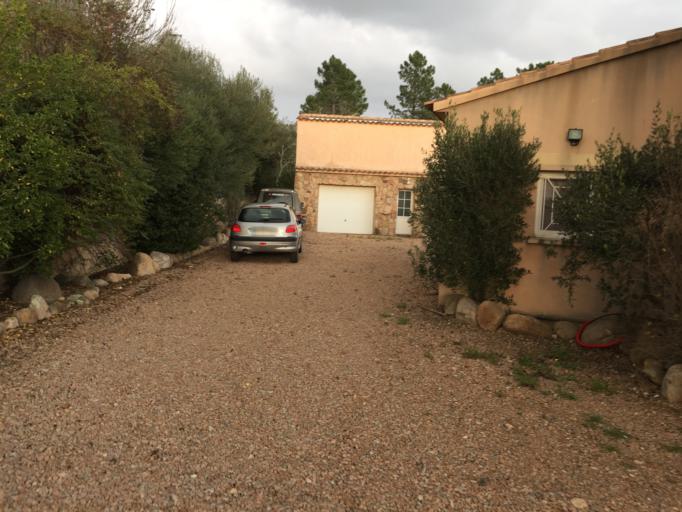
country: FR
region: Corsica
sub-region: Departement de la Corse-du-Sud
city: Porto-Vecchio
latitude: 41.6506
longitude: 9.3027
